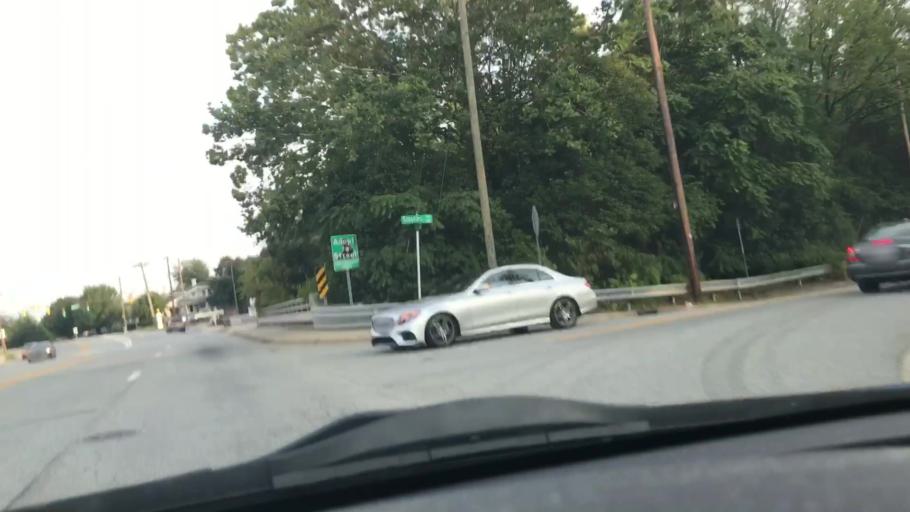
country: US
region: North Carolina
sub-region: Guilford County
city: Greensboro
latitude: 36.0762
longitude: -79.8171
